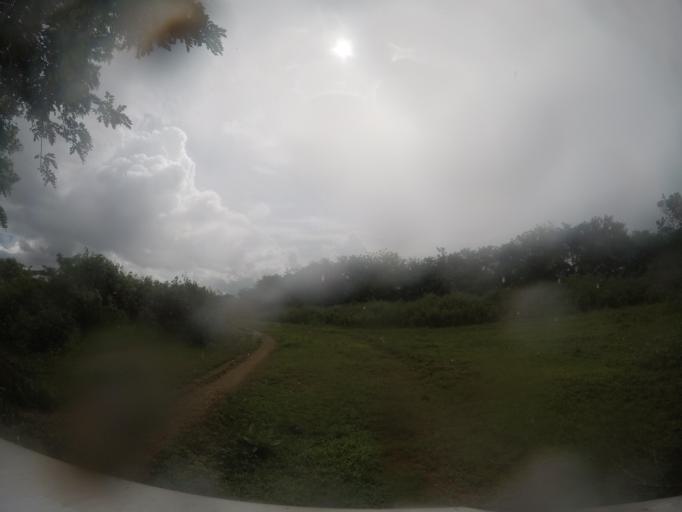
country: TL
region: Lautem
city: Lospalos
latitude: -8.5071
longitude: 127.0100
